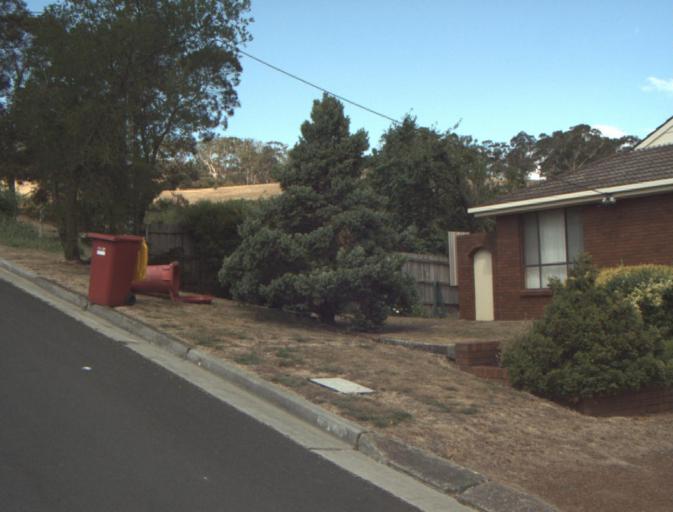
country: AU
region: Tasmania
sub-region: Launceston
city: Newstead
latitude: -41.4547
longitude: 147.2078
